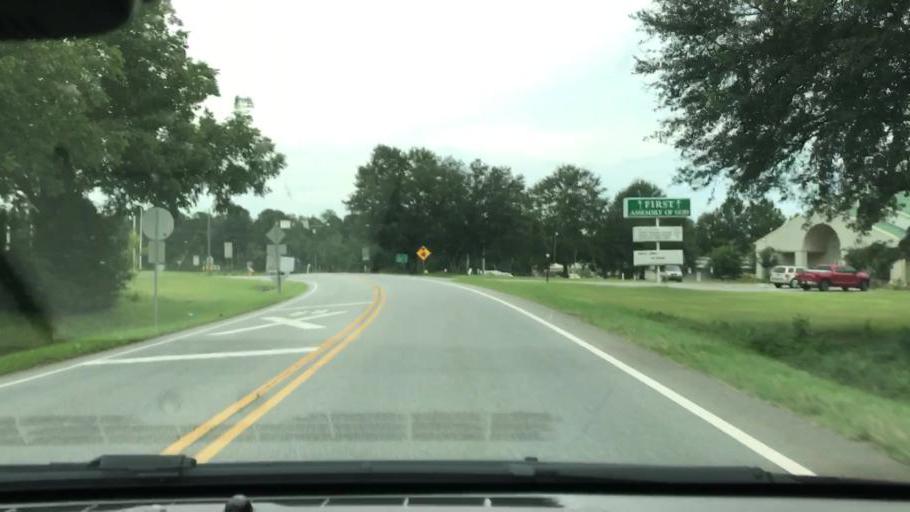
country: US
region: Georgia
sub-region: Early County
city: Blakely
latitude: 31.3705
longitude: -84.9578
